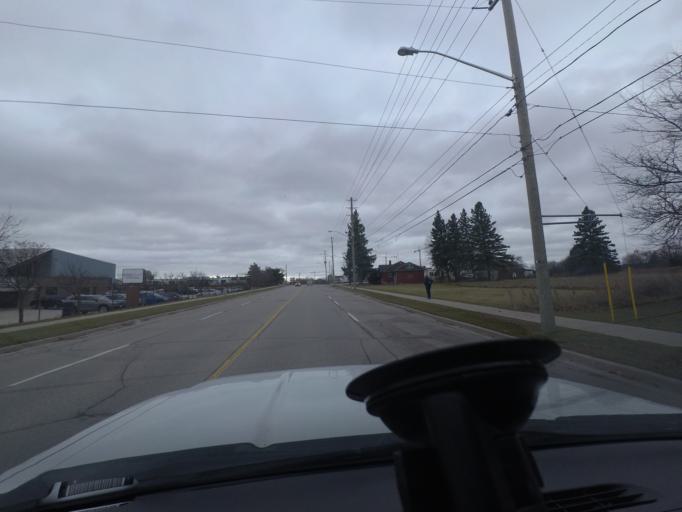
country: CN
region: Xinjiang Uygur Zizhiqu
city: Ayxin Siri
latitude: 43.4841
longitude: 80.5394
